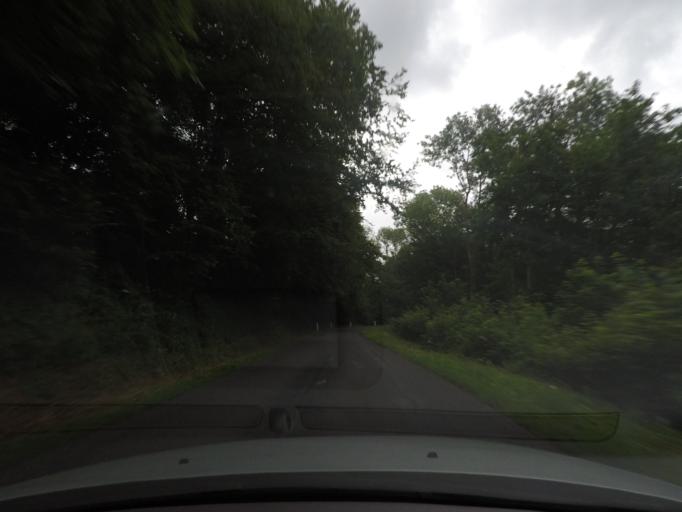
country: FR
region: Haute-Normandie
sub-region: Departement de la Seine-Maritime
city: Neufchatel-en-Bray
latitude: 49.7395
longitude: 1.4797
